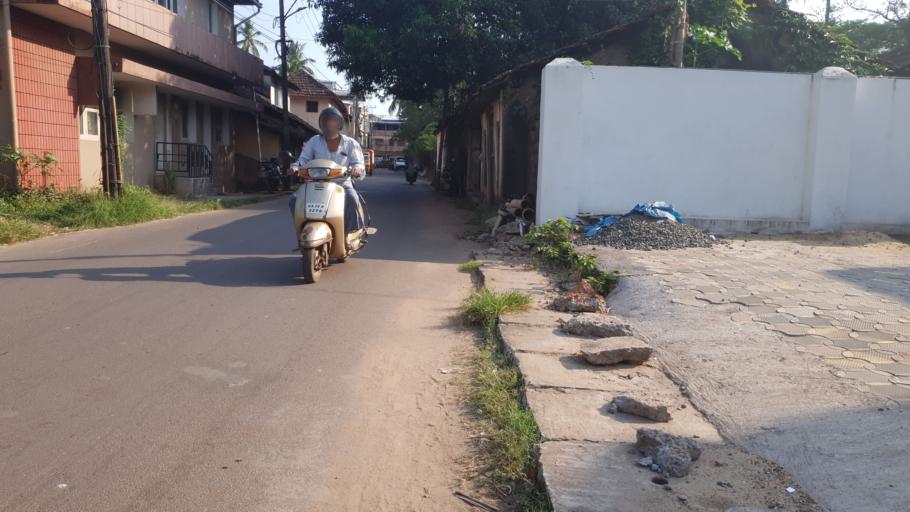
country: IN
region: Karnataka
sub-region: Dakshina Kannada
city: Mangalore
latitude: 12.8716
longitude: 74.8318
